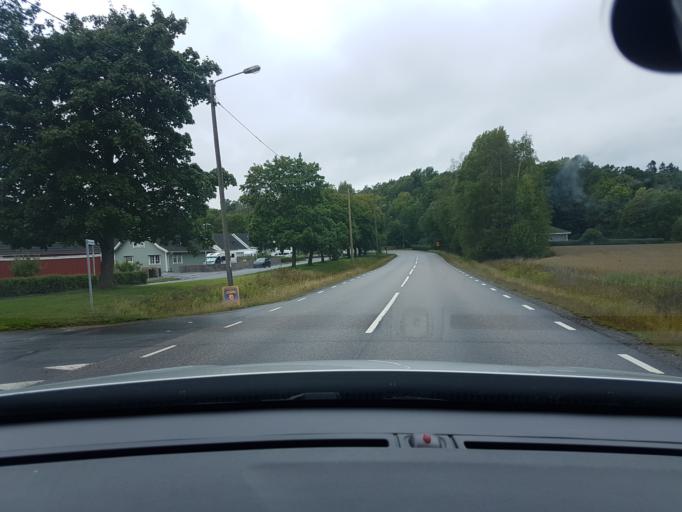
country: SE
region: Vaestra Goetaland
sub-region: Ale Kommun
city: Salanda
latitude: 57.9840
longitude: 12.2213
